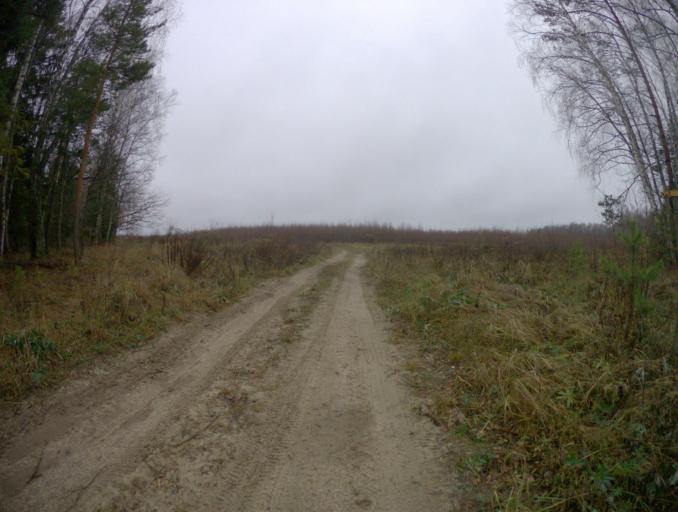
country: RU
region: Vladimir
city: Golovino
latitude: 55.9902
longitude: 40.4468
